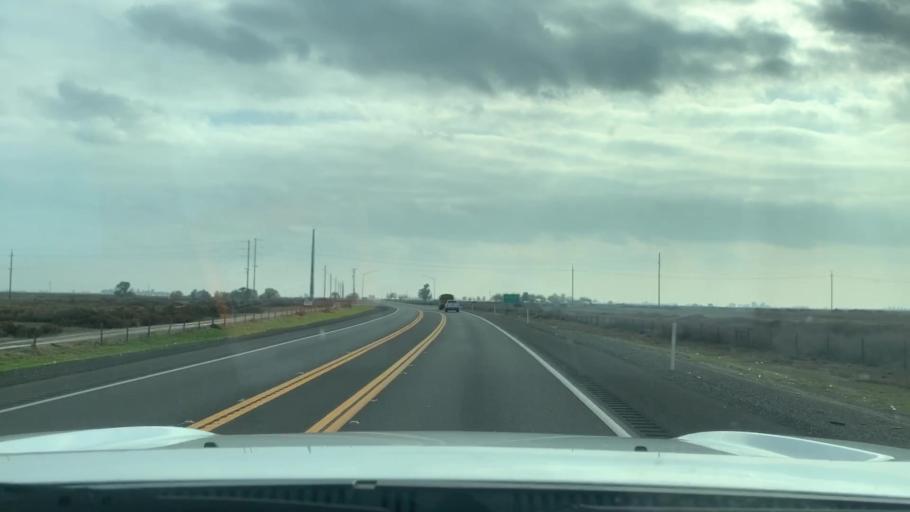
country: US
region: California
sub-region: Kings County
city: Stratford
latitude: 36.2430
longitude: -119.8164
